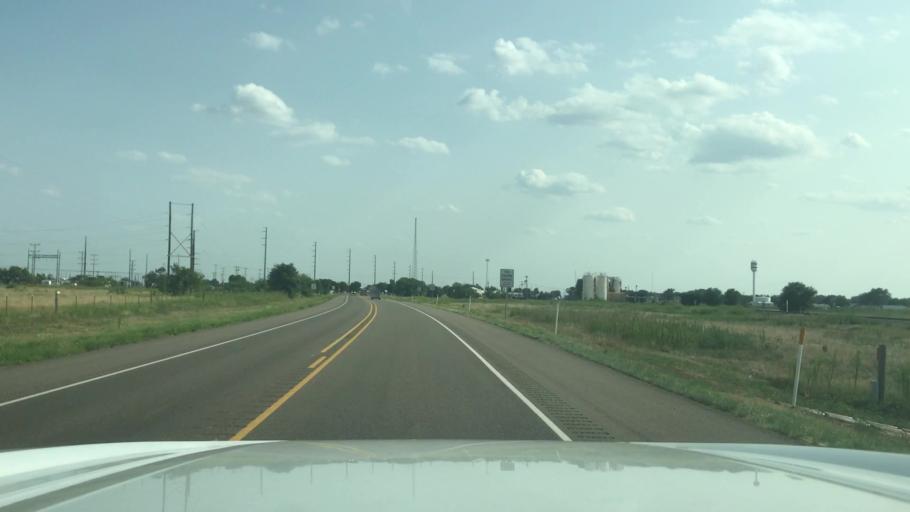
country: US
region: Texas
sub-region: Hartley County
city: Channing
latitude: 35.6938
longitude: -102.3282
